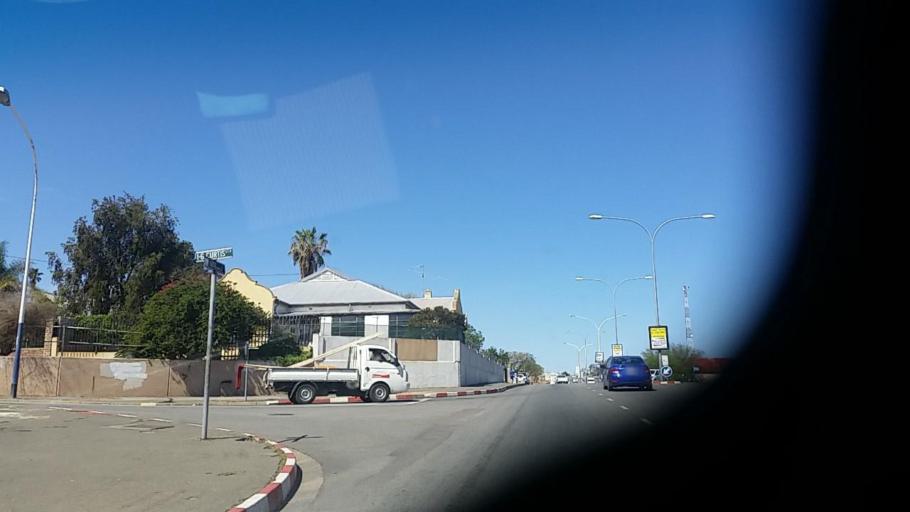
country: ZA
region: Western Cape
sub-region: Eden District Municipality
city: Oudtshoorn
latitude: -33.5940
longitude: 22.2116
